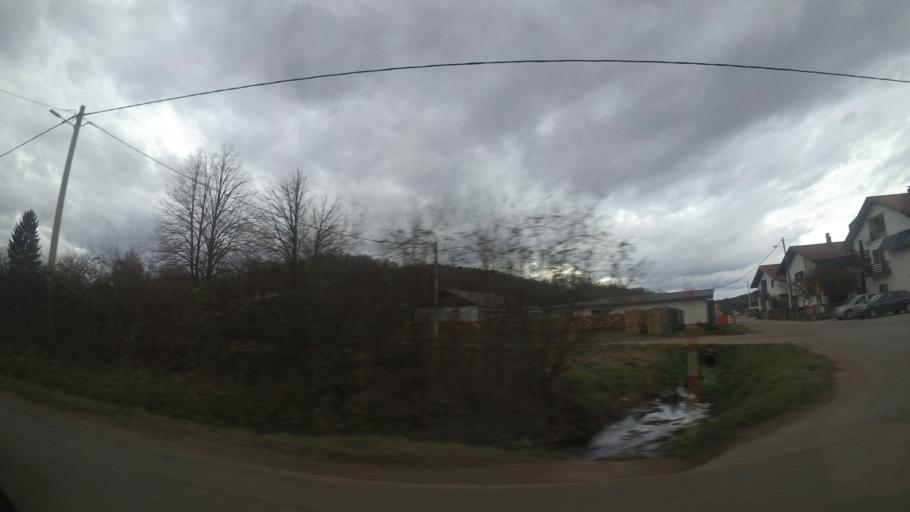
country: HR
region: Karlovacka
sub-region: Grad Karlovac
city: Karlovac
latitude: 45.4420
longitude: 15.5535
